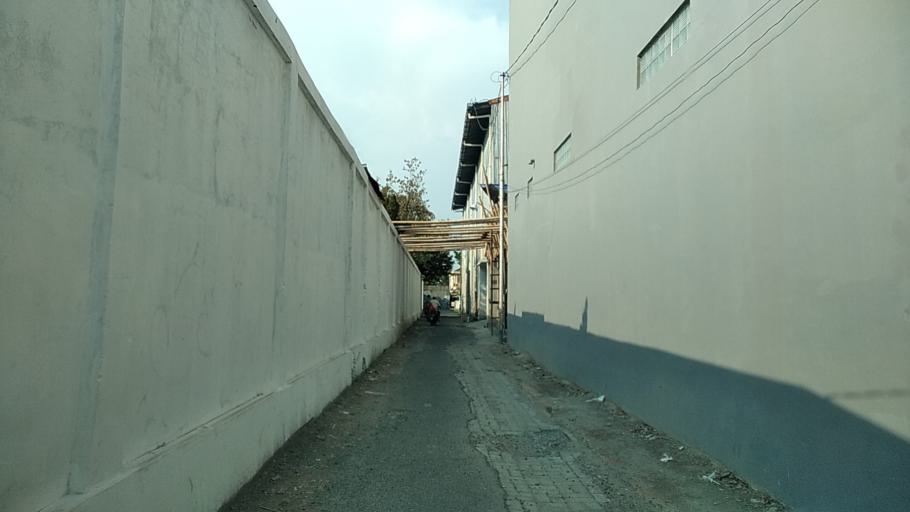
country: ID
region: Central Java
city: Semarang
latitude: -7.0062
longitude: 110.4562
